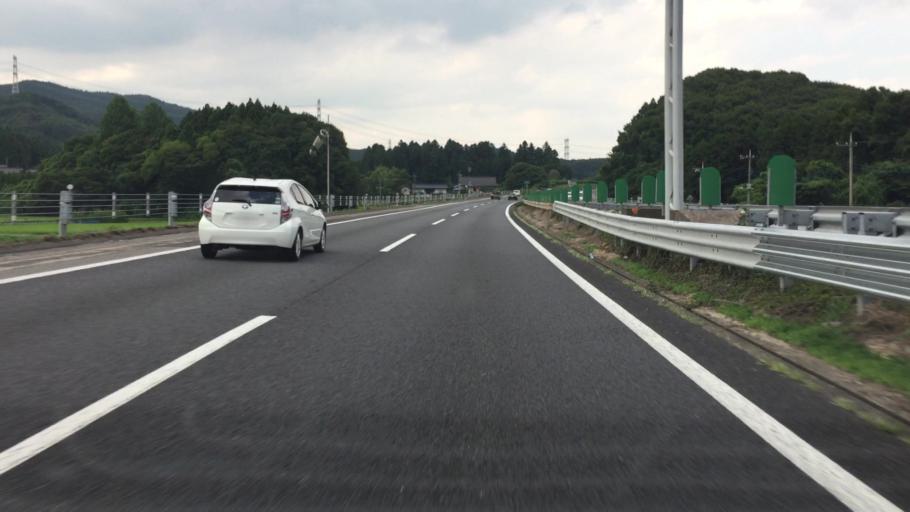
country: JP
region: Tochigi
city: Utsunomiya-shi
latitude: 36.6471
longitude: 139.8553
